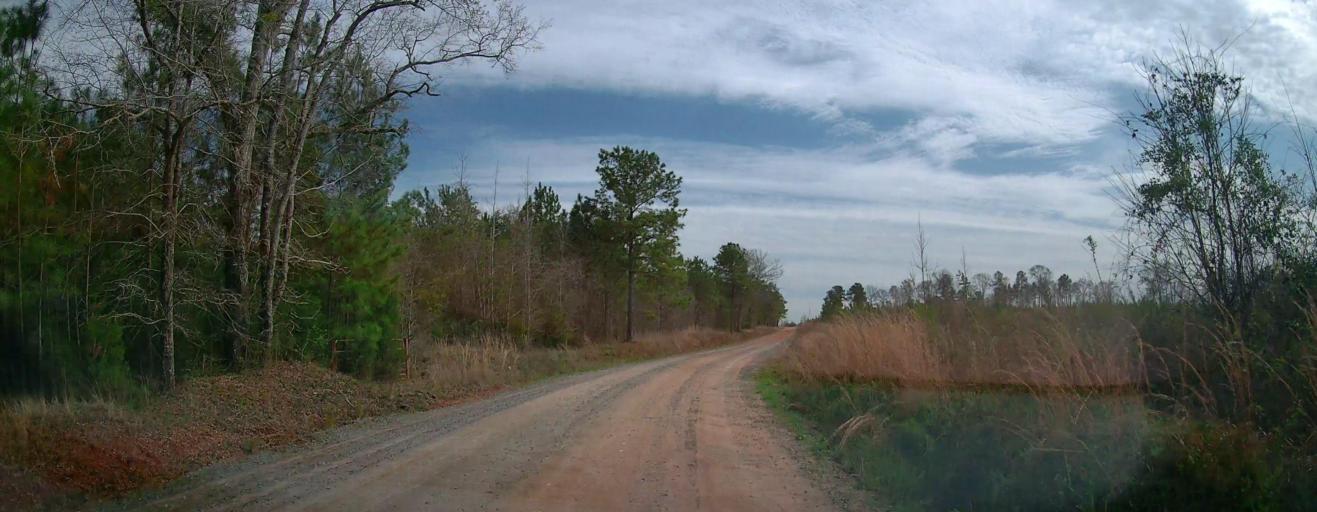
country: US
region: Georgia
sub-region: Monroe County
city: Forsyth
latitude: 33.0362
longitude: -83.8831
